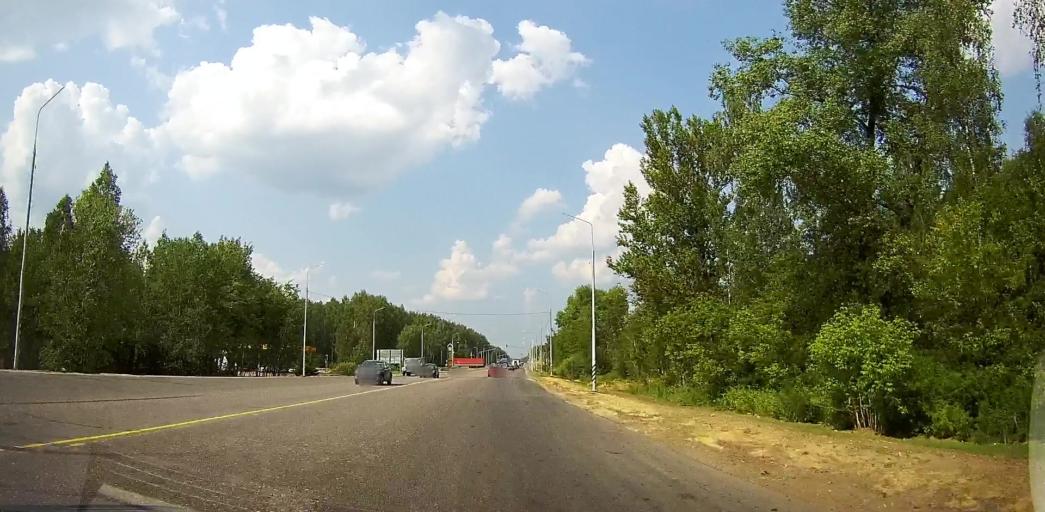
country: RU
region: Moskovskaya
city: Mikhnevo
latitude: 55.0750
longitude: 37.9515
